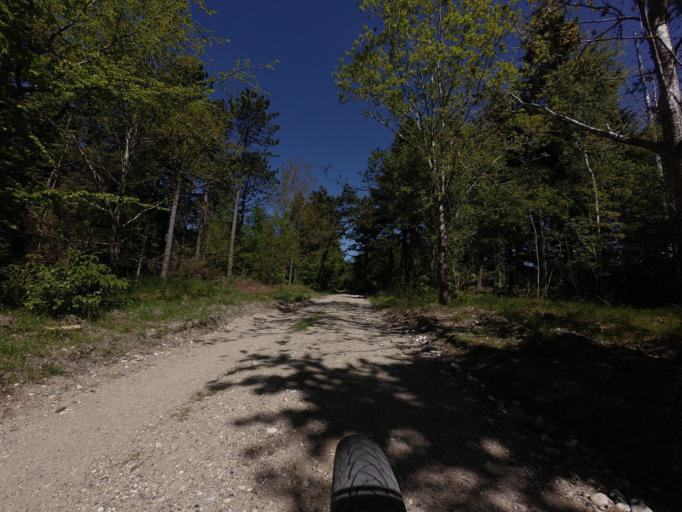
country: DK
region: North Denmark
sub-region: Jammerbugt Kommune
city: Pandrup
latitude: 57.2457
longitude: 9.6056
